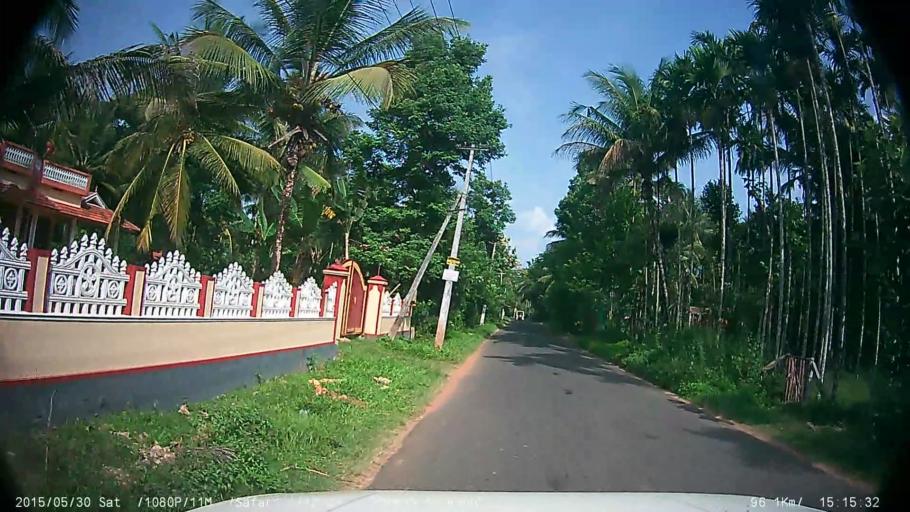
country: IN
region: Kerala
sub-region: Wayanad
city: Panamaram
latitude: 11.7793
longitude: 76.0501
